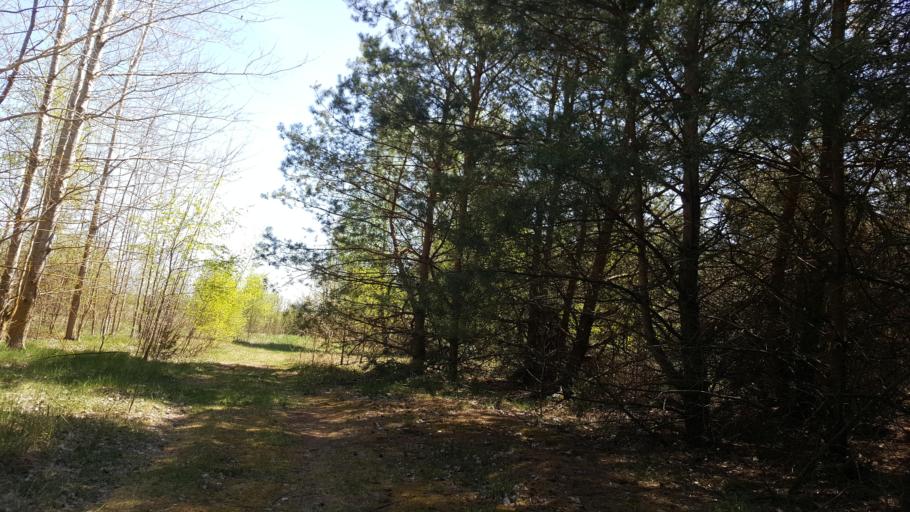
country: BY
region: Brest
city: Kamyanyets
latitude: 52.4261
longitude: 23.8542
